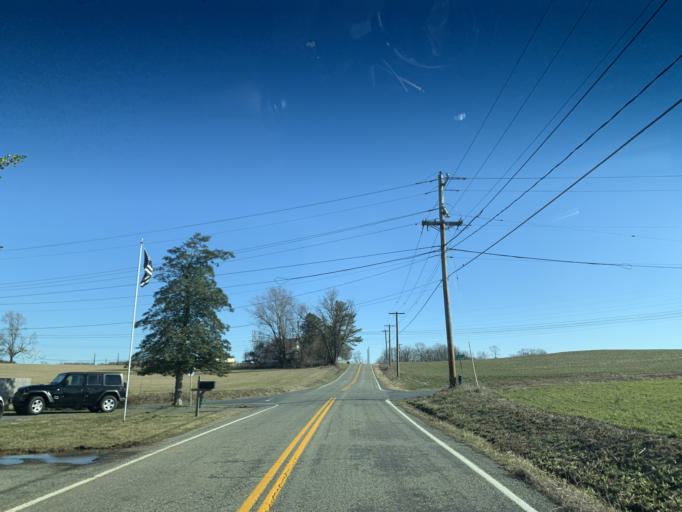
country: US
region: Maryland
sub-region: Cecil County
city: Rising Sun
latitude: 39.6821
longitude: -76.1006
